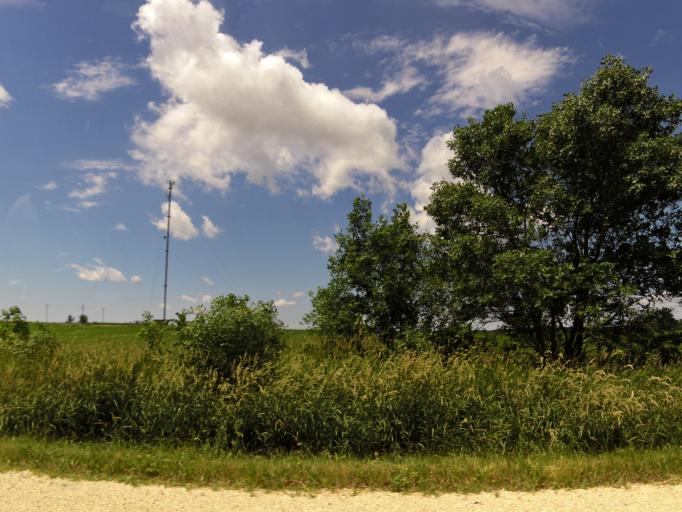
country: US
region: Iowa
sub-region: Fayette County
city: Oelwein
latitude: 42.6944
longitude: -91.9133
